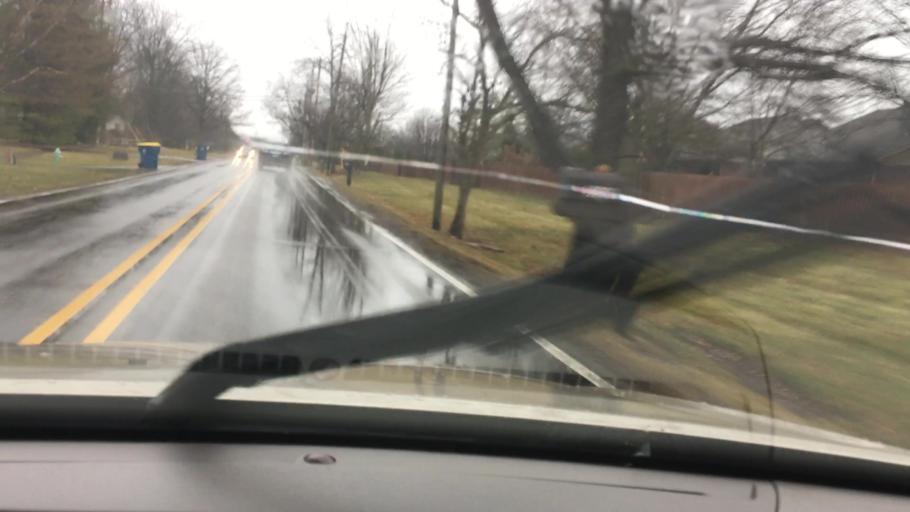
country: US
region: Indiana
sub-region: Marion County
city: Broad Ripple
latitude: 39.8833
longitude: -86.0789
